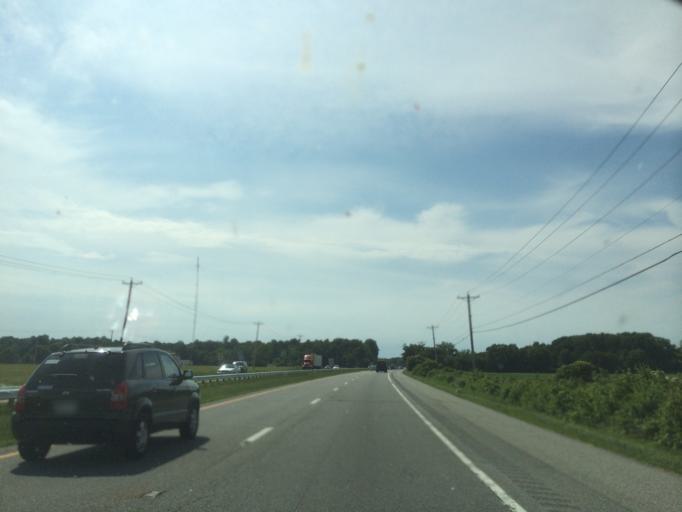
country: US
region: Maryland
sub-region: Queen Anne's County
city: Centreville
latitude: 38.9578
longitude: -76.0901
